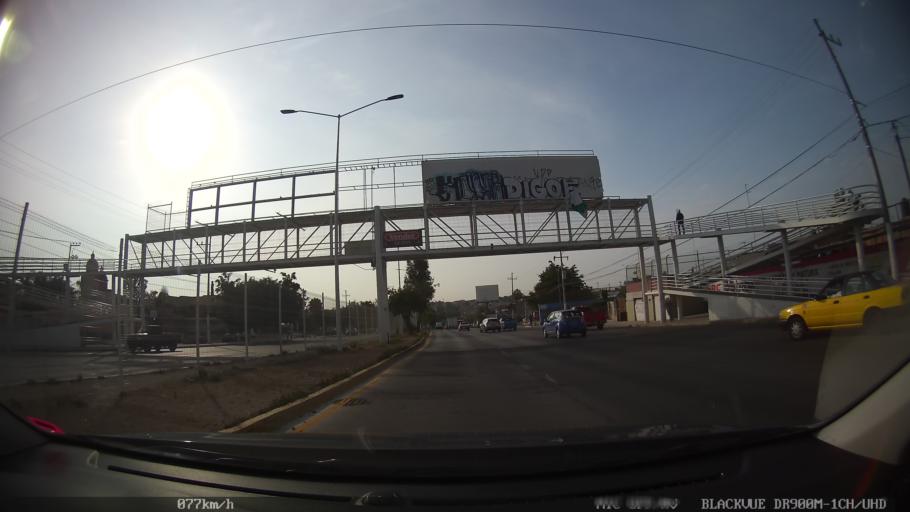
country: MX
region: Jalisco
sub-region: Zapopan
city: Zapopan
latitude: 20.7269
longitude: -103.3409
